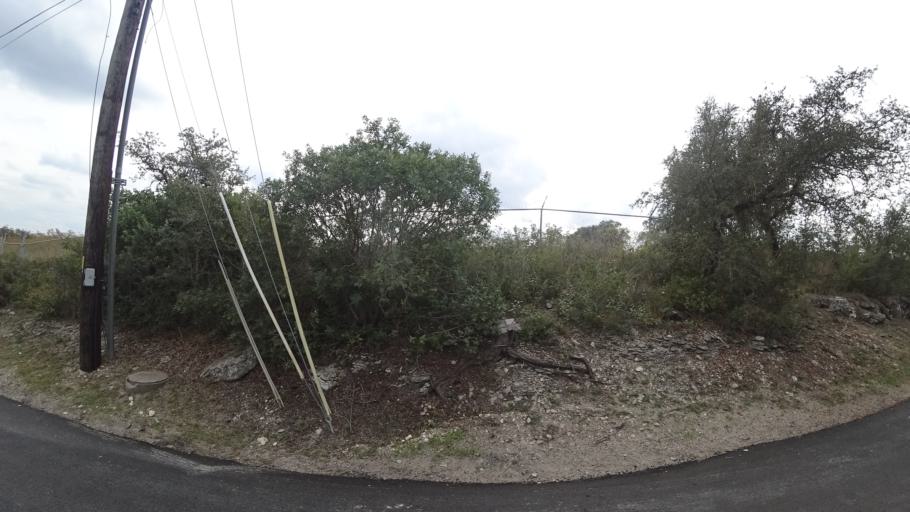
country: US
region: Texas
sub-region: Travis County
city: Hudson Bend
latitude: 30.3921
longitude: -97.8809
